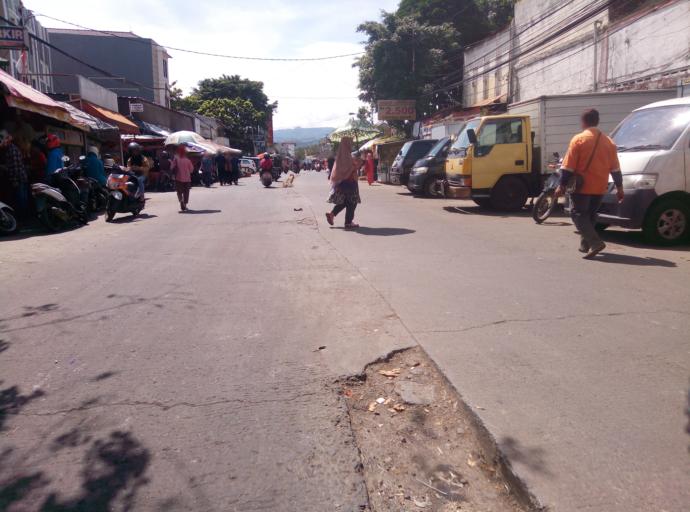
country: ID
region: West Java
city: Bandung
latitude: -6.9079
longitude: 107.6438
